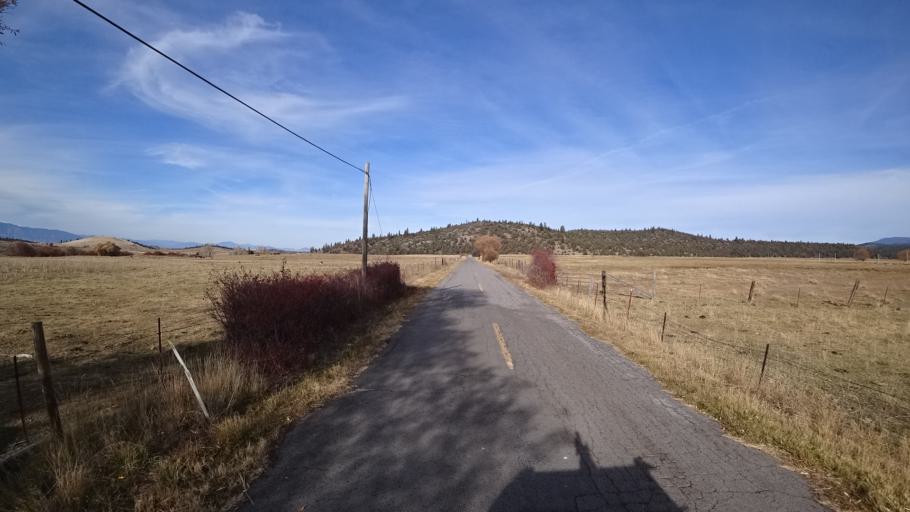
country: US
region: California
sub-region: Siskiyou County
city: Weed
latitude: 41.4586
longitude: -122.3847
